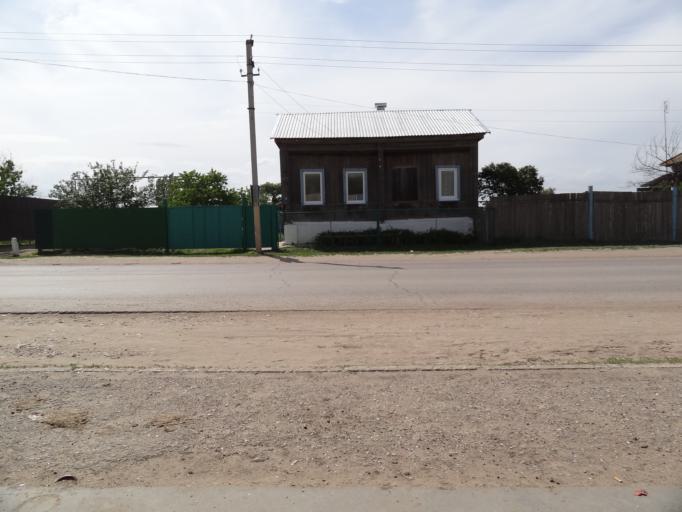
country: RU
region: Saratov
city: Privolzhskiy
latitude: 51.2062
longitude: 45.9180
